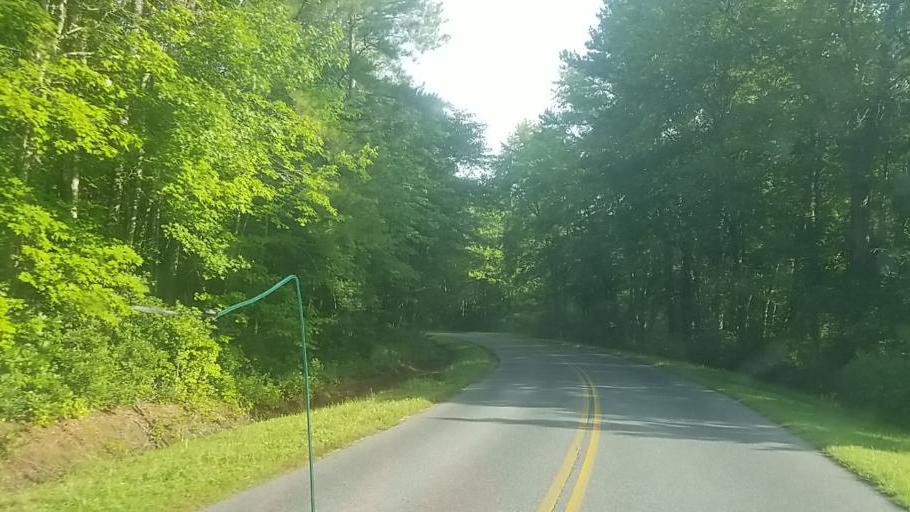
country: US
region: Maryland
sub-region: Worcester County
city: West Ocean City
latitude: 38.3207
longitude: -75.1468
